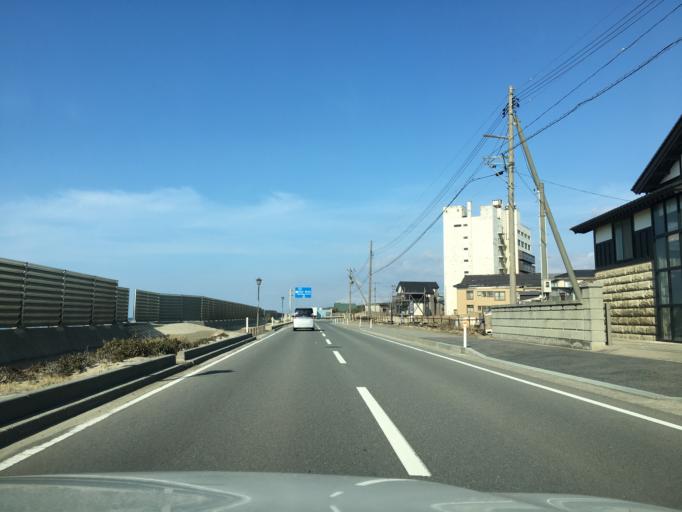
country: JP
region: Yamagata
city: Tsuruoka
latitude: 38.7830
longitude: 139.7528
